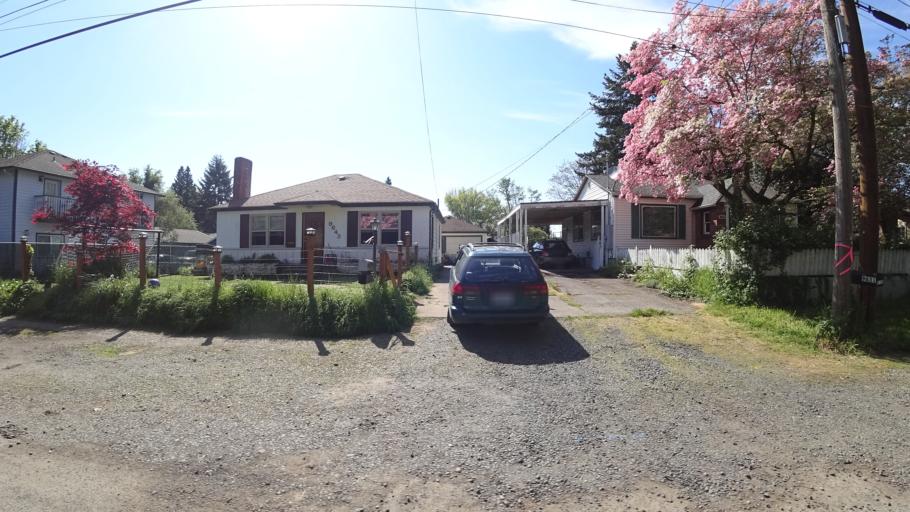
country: US
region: Oregon
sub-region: Clackamas County
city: Milwaukie
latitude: 45.4532
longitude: -122.6235
